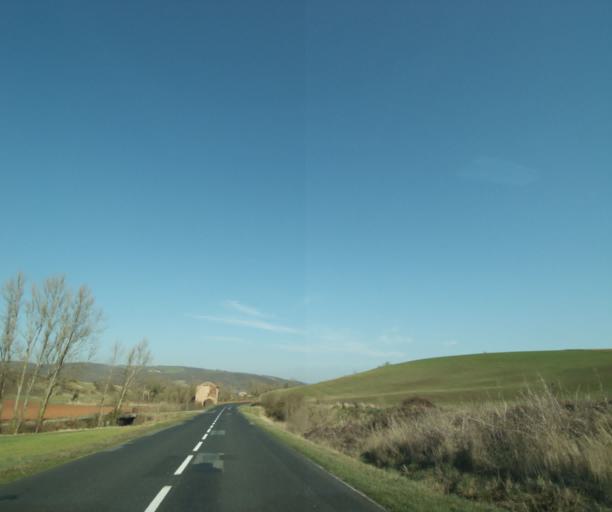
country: FR
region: Midi-Pyrenees
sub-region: Departement de l'Aveyron
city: Camares
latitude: 43.8773
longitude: 2.8201
